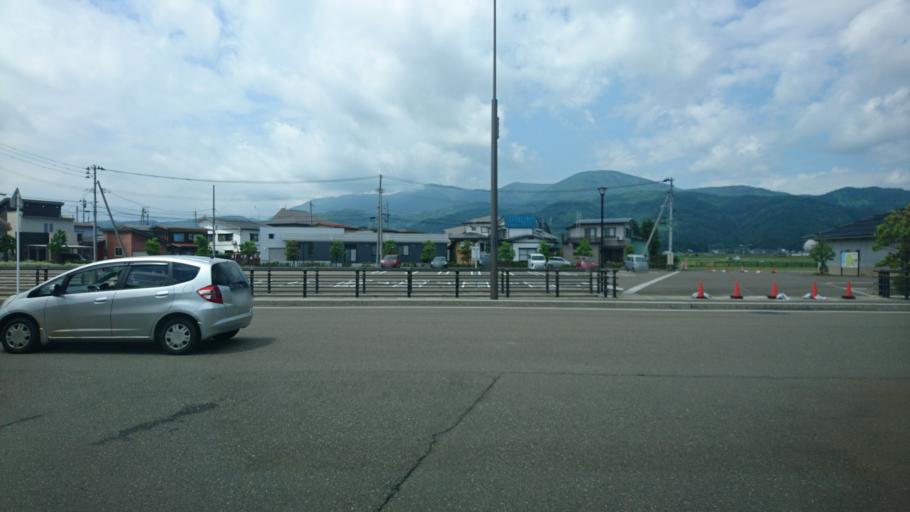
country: JP
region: Niigata
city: Joetsu
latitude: 37.0809
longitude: 138.2463
